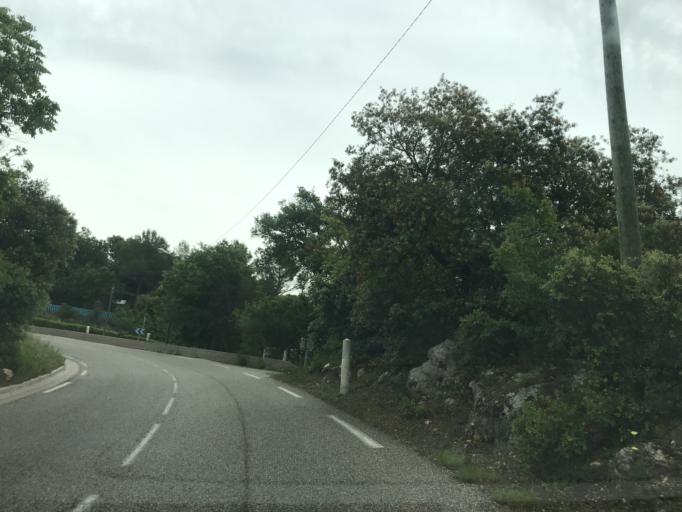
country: FR
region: Provence-Alpes-Cote d'Azur
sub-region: Departement du Var
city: Ginasservis
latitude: 43.6637
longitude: 5.8520
